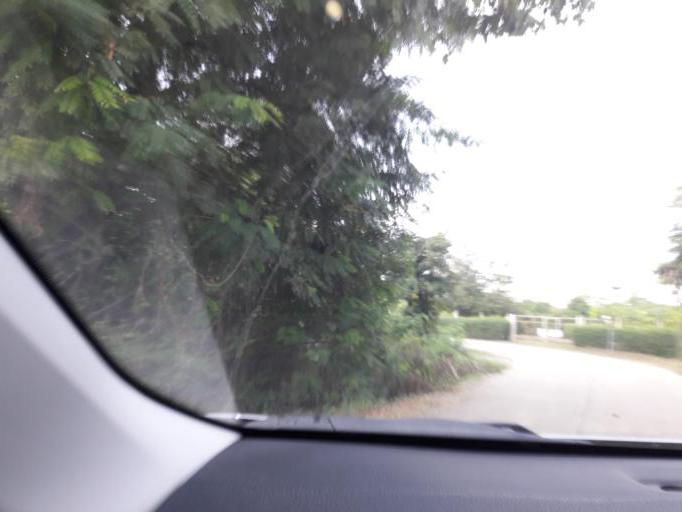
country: TH
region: Ang Thong
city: Ang Thong
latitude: 14.5500
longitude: 100.4423
